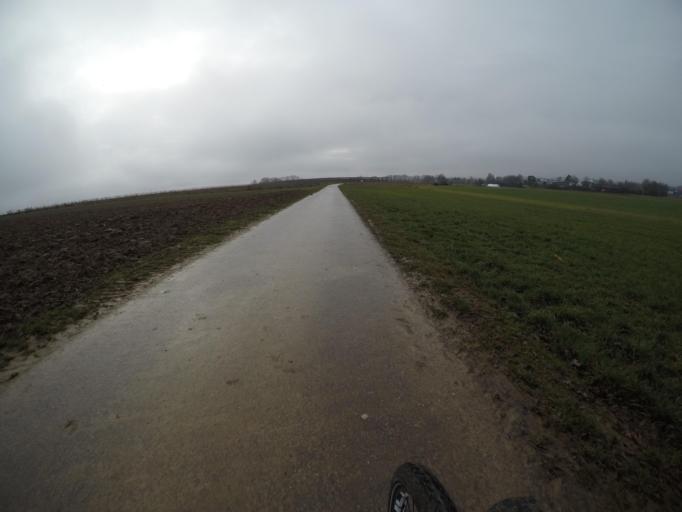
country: DE
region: Baden-Wuerttemberg
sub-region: Regierungsbezirk Stuttgart
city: Wolfschlugen
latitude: 48.6477
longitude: 9.2603
